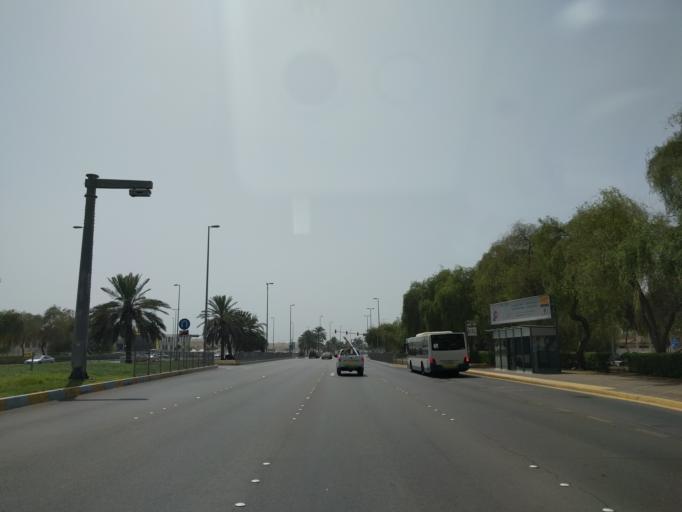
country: AE
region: Abu Dhabi
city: Abu Dhabi
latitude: 24.4410
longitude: 54.4087
